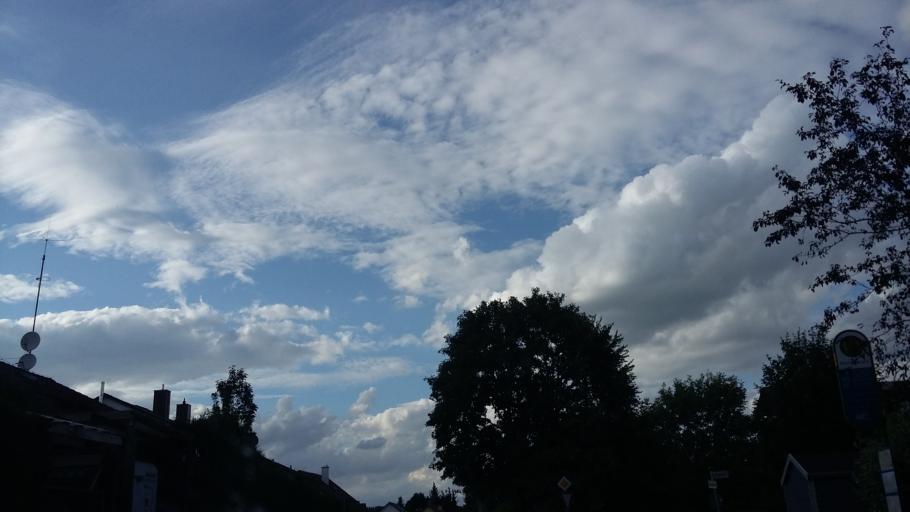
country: DE
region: Bavaria
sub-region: Upper Bavaria
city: Mittelstetten
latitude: 48.2520
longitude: 11.0970
